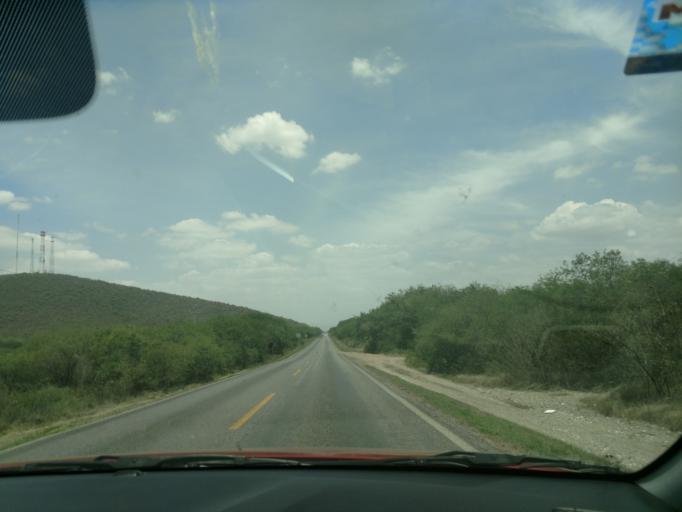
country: MX
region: San Luis Potosi
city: Ciudad Fernandez
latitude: 21.9834
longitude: -100.1154
